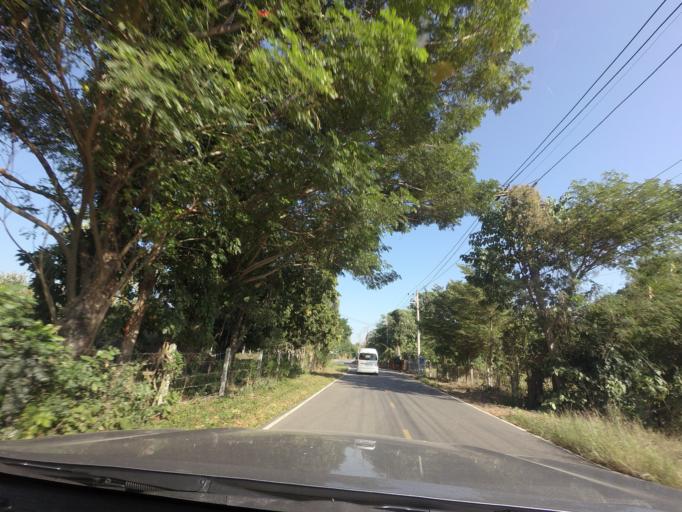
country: TH
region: Sukhothai
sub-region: Amphoe Si Satchanalai
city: Si Satchanalai
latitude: 17.4311
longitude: 99.7952
